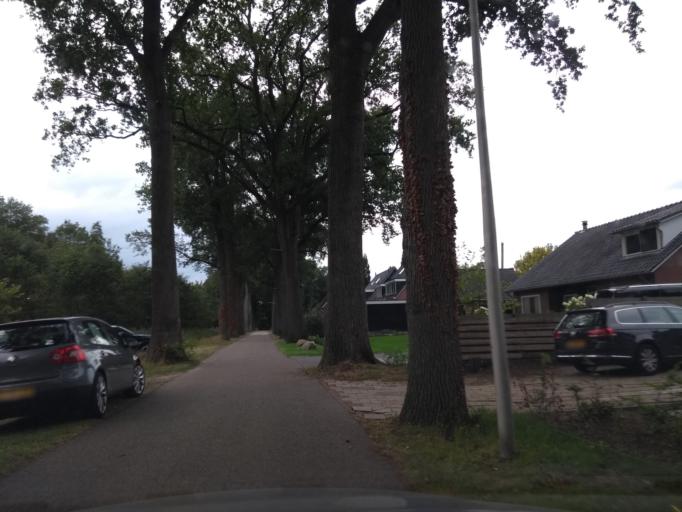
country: NL
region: Overijssel
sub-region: Gemeente Oldenzaal
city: Oldenzaal
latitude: 52.3726
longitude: 6.9981
